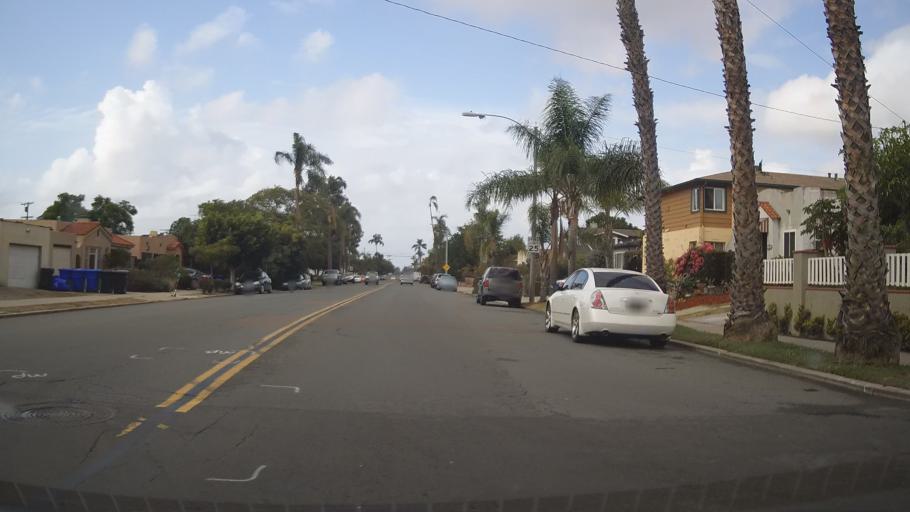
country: US
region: California
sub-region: San Diego County
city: San Diego
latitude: 32.7297
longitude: -117.1254
